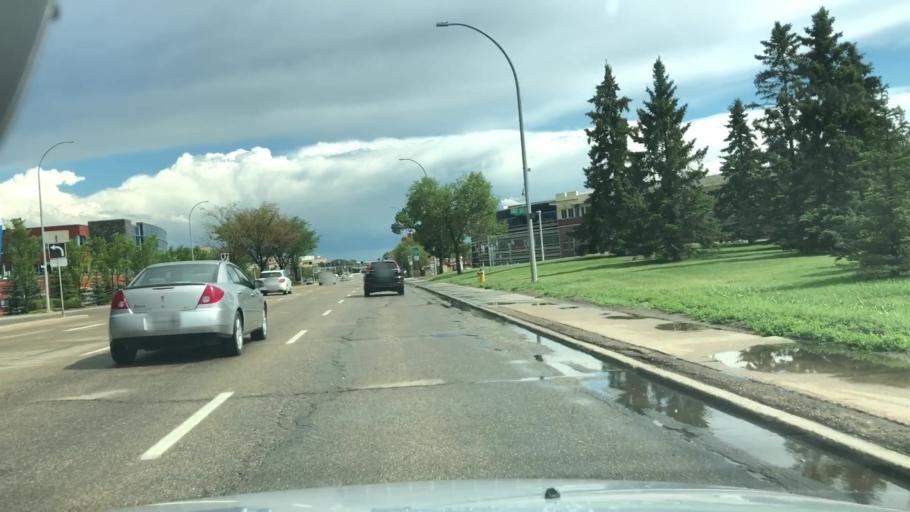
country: CA
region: Alberta
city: Edmonton
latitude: 53.5620
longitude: -113.5114
